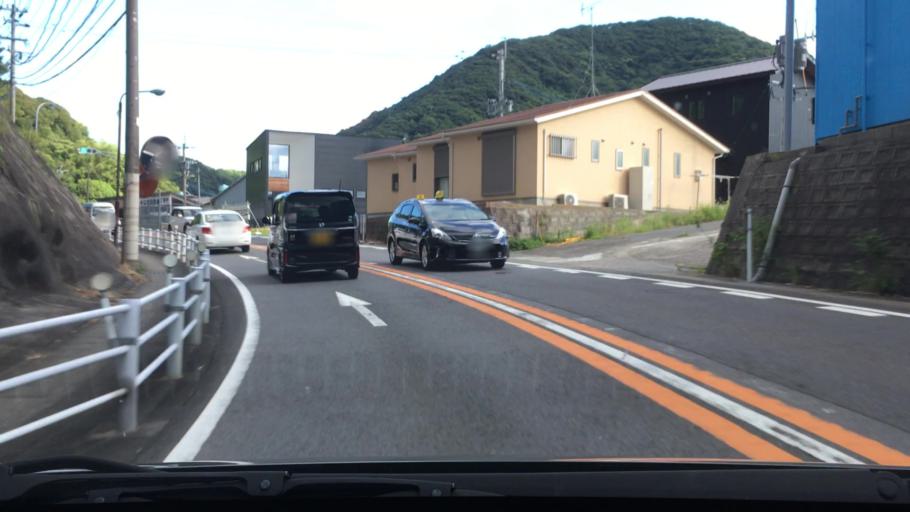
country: JP
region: Nagasaki
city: Togitsu
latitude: 32.8120
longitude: 129.8089
